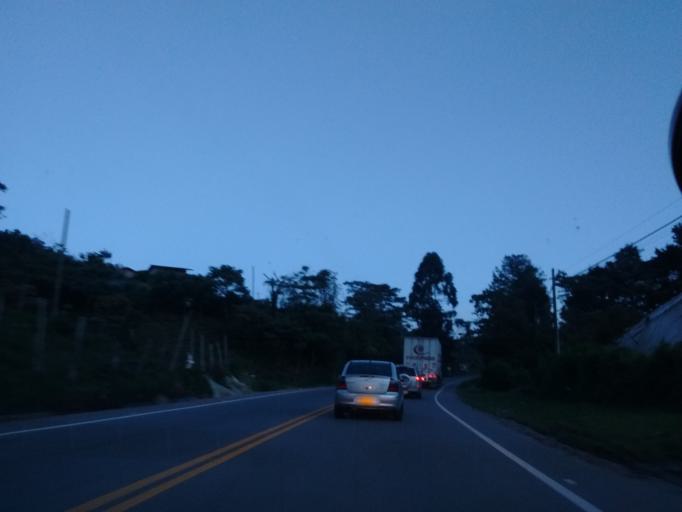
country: CO
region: Antioquia
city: Santuario
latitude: 6.1177
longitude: -75.2329
